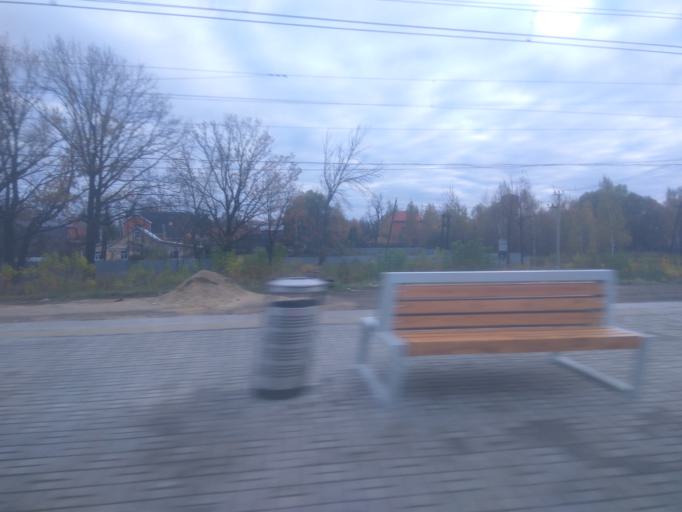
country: RU
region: Moskovskaya
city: Aprelevka
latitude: 55.5783
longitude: 37.1109
